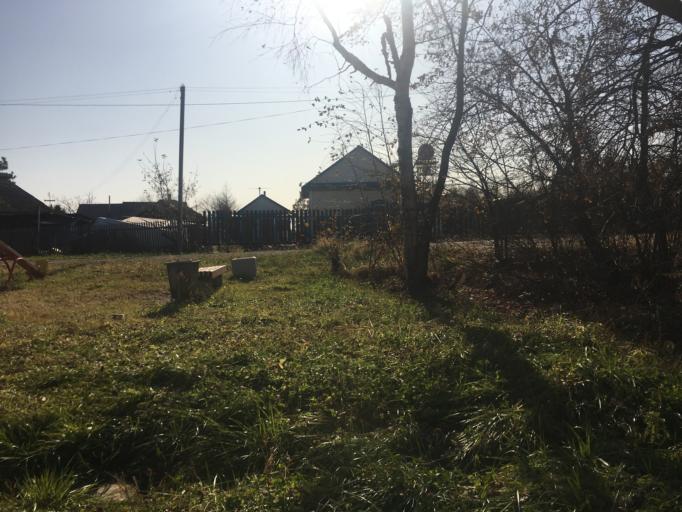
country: RU
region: Primorskiy
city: Dal'nerechensk
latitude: 45.8811
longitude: 133.7274
